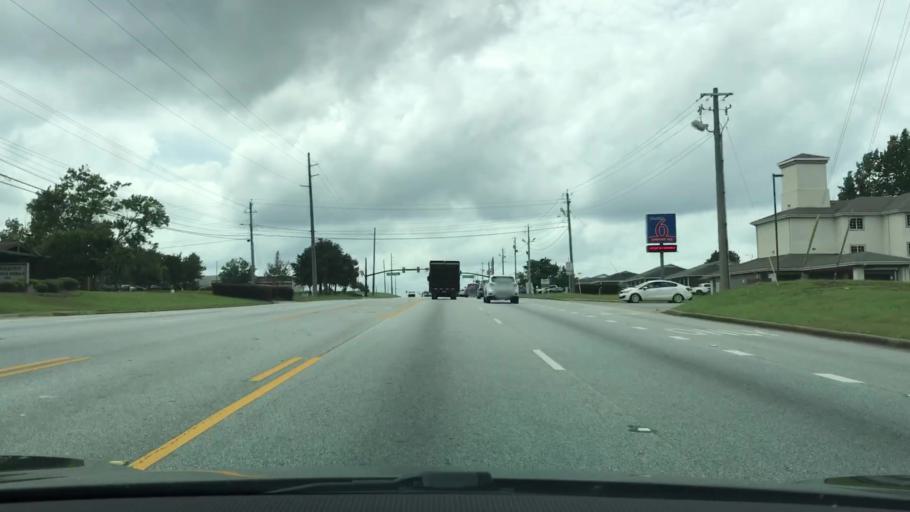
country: US
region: Alabama
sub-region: Lee County
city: Opelika
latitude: 32.6276
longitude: -85.4052
